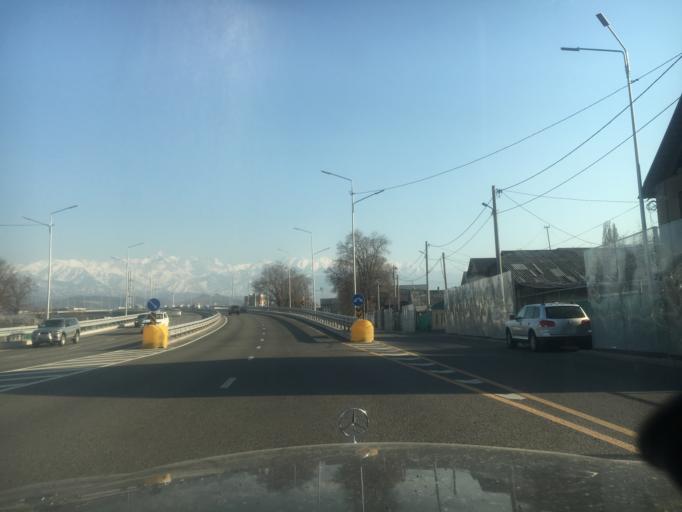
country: KZ
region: Almaty Qalasy
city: Almaty
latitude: 43.2792
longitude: 76.9404
